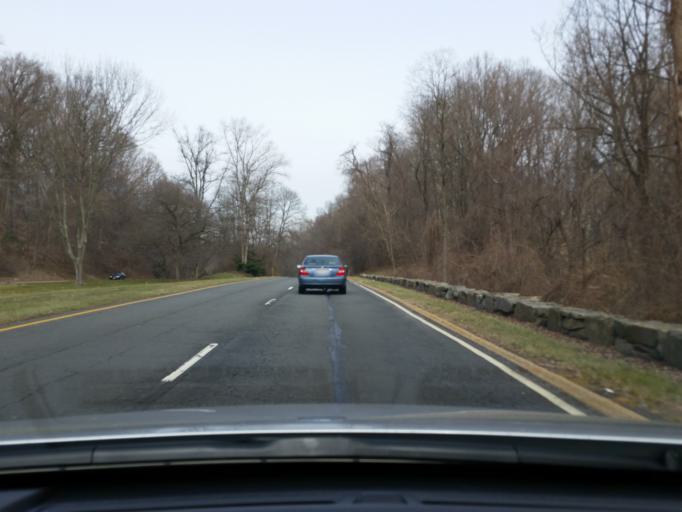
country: US
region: Maryland
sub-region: Montgomery County
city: Brookmont
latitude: 38.9493
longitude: -77.1371
